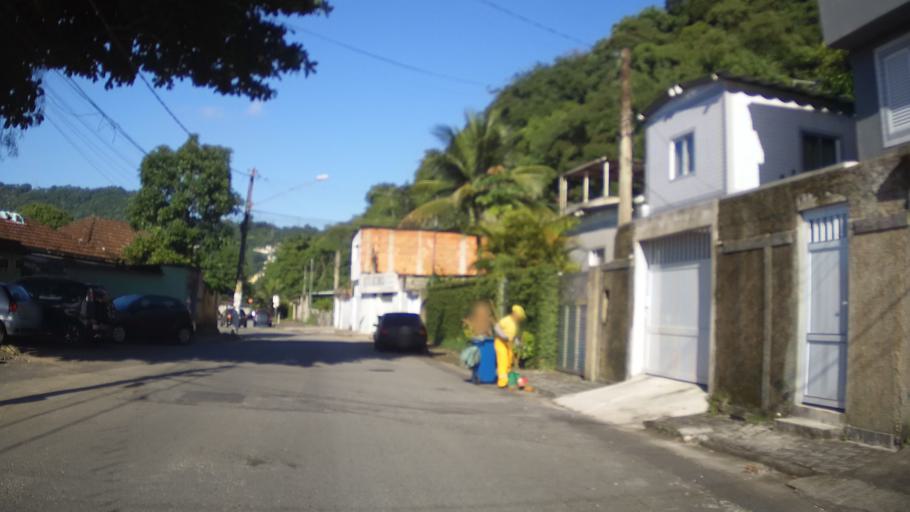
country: BR
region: Sao Paulo
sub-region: Santos
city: Santos
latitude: -23.9497
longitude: -46.3446
